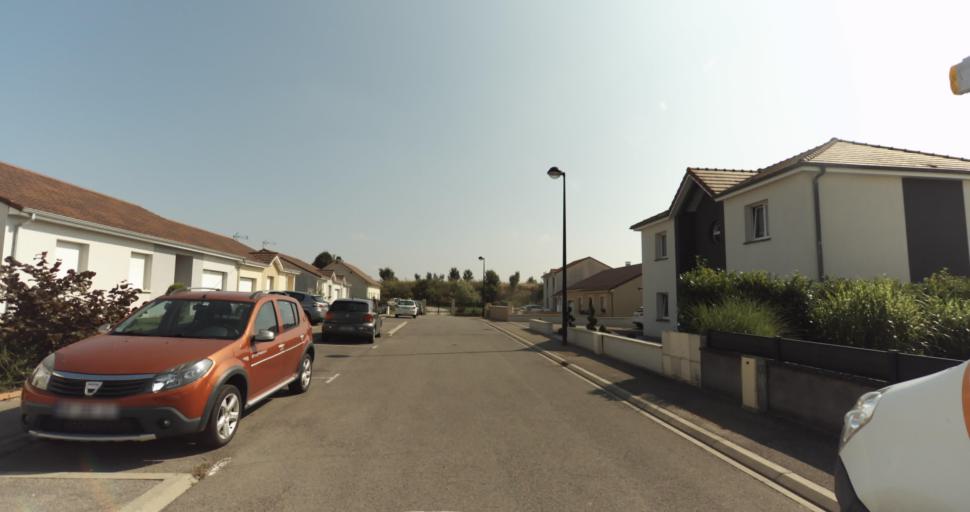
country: FR
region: Lorraine
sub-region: Departement de Meurthe-et-Moselle
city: Briey
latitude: 49.2525
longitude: 5.9501
